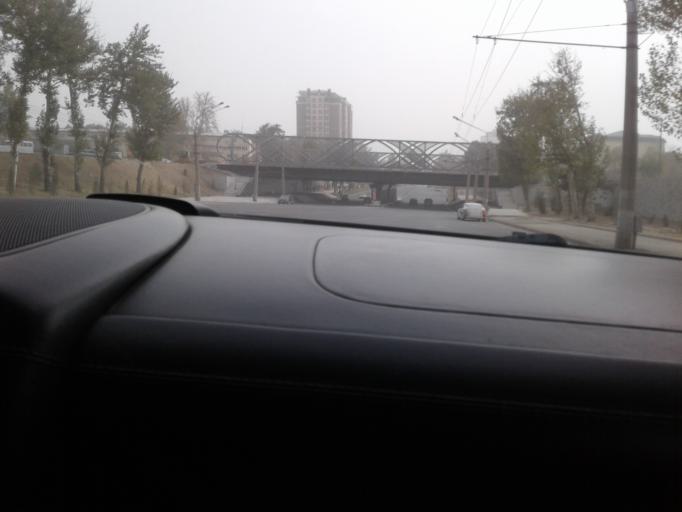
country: TJ
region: Dushanbe
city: Dushanbe
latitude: 38.5705
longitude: 68.7546
